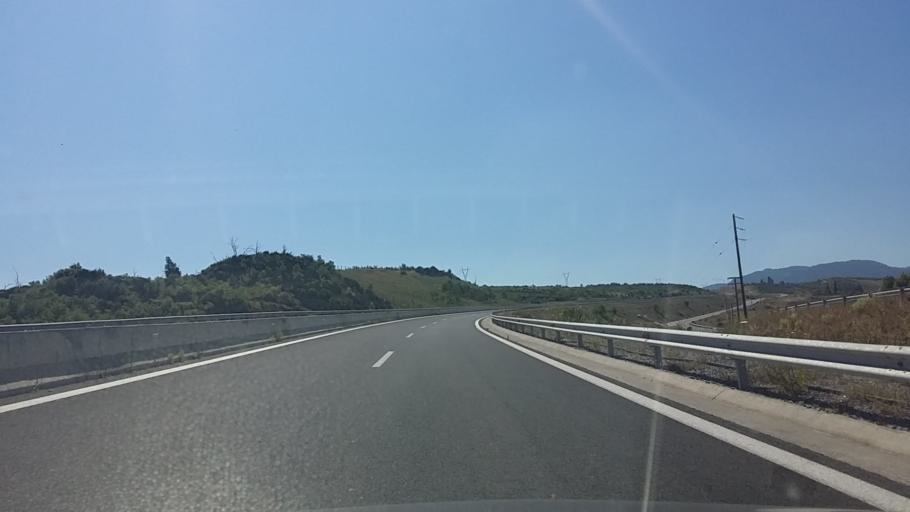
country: GR
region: Peloponnese
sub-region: Nomos Arkadias
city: Megalopoli
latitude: 37.3301
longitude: 22.1599
